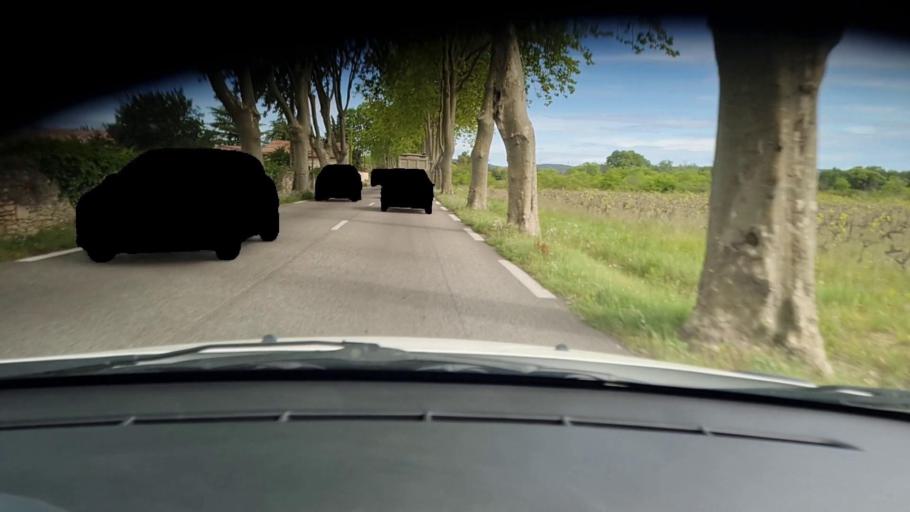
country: FR
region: Languedoc-Roussillon
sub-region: Departement du Gard
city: Remoulins
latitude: 43.9488
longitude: 4.5691
